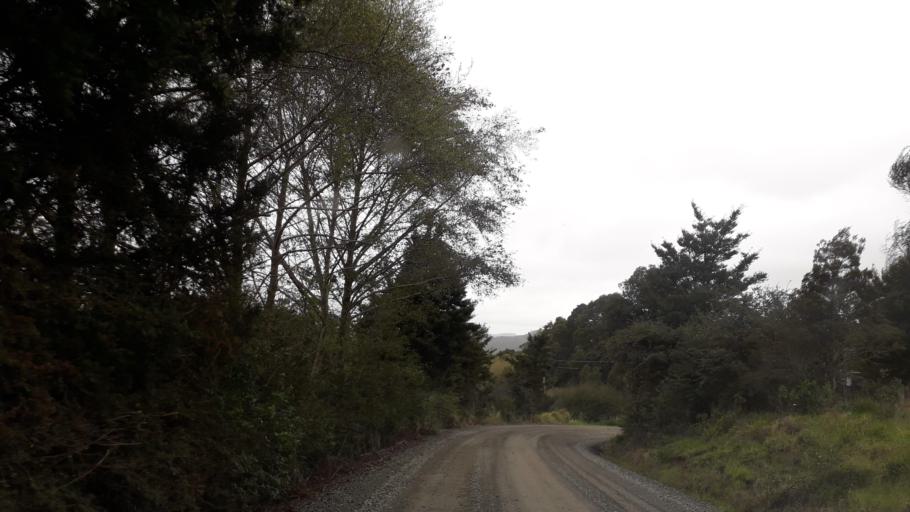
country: NZ
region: Northland
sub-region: Far North District
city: Kerikeri
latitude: -35.1213
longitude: 173.7490
